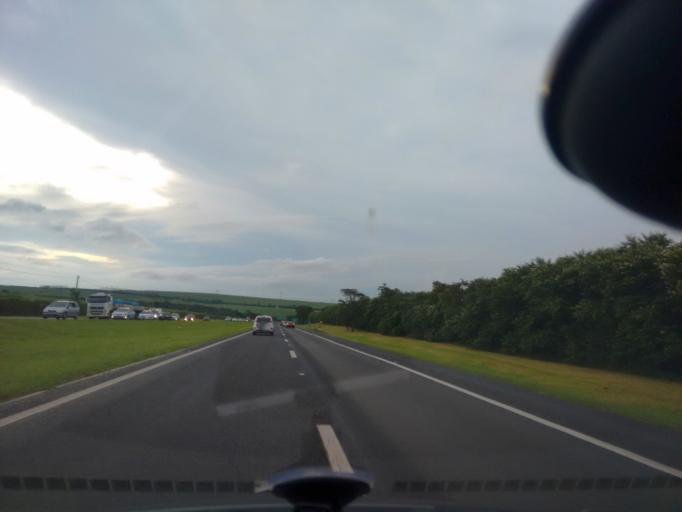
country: BR
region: Sao Paulo
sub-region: Itirapina
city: Itirapina
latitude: -22.2249
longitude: -47.7535
